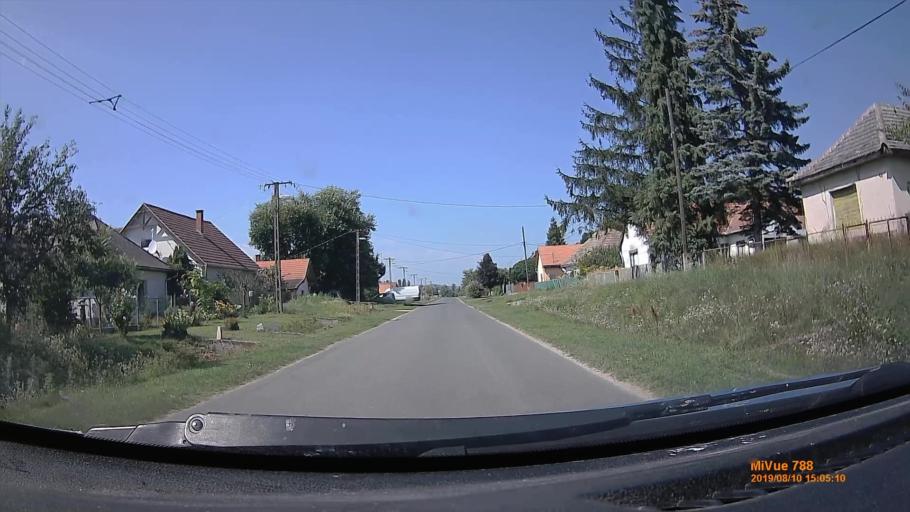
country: HU
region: Somogy
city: Fonyod
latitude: 46.6786
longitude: 17.5653
